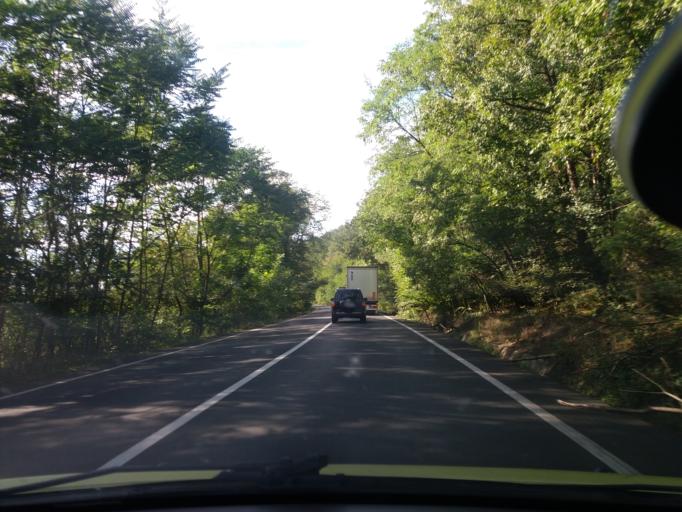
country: RO
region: Arad
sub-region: Comuna Savarsin
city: Savarsin
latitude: 46.0120
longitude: 22.2677
